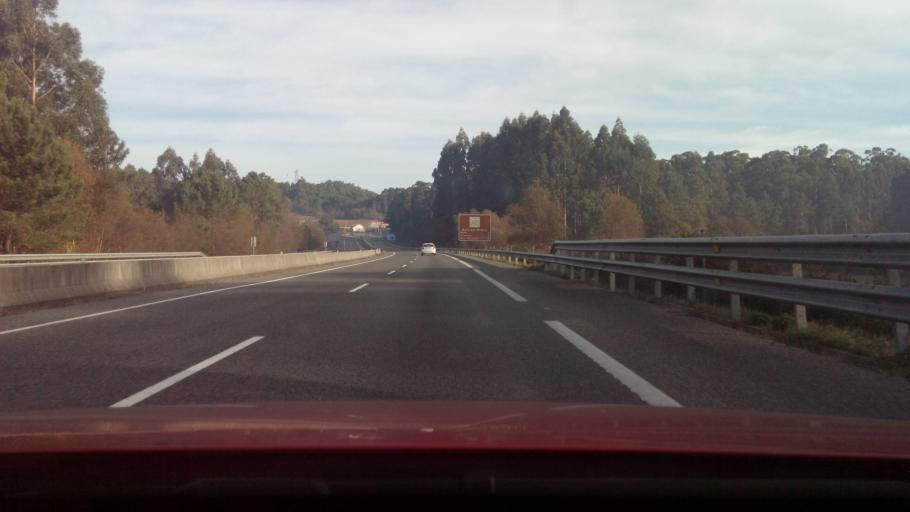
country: ES
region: Galicia
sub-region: Provincia de Pontevedra
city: Meano
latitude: 42.4387
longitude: -8.8008
